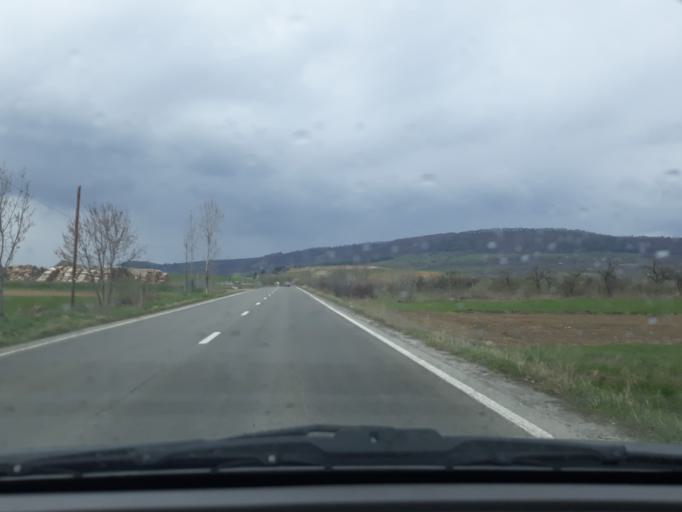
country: RO
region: Harghita
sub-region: Comuna Lupeni
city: Lupeni
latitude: 46.3892
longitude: 25.2161
